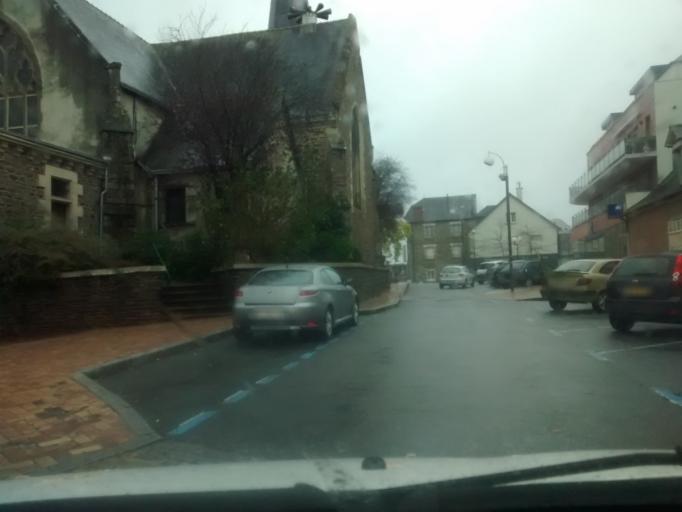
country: FR
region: Brittany
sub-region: Departement d'Ille-et-Vilaine
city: Chantepie
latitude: 48.0884
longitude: -1.6168
